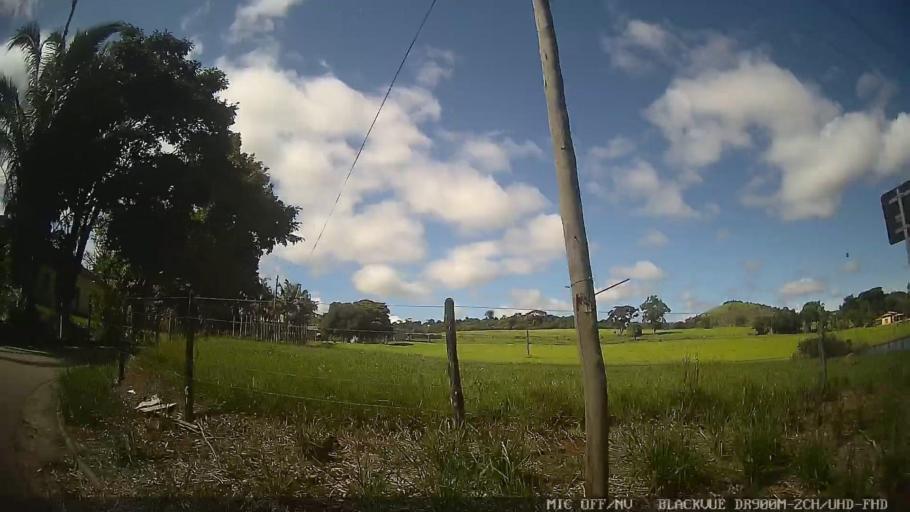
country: BR
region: Sao Paulo
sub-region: Amparo
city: Amparo
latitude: -22.8564
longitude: -46.7719
